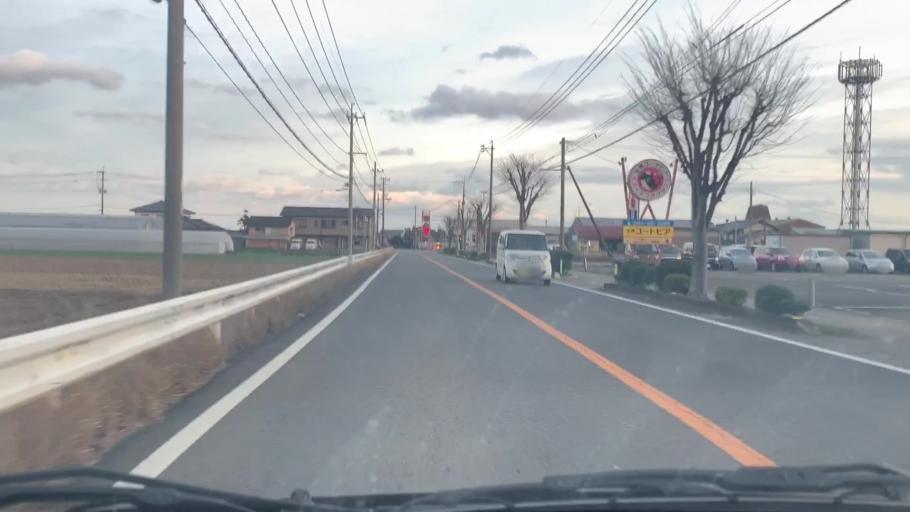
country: JP
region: Saga Prefecture
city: Kashima
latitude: 33.1250
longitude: 130.0702
